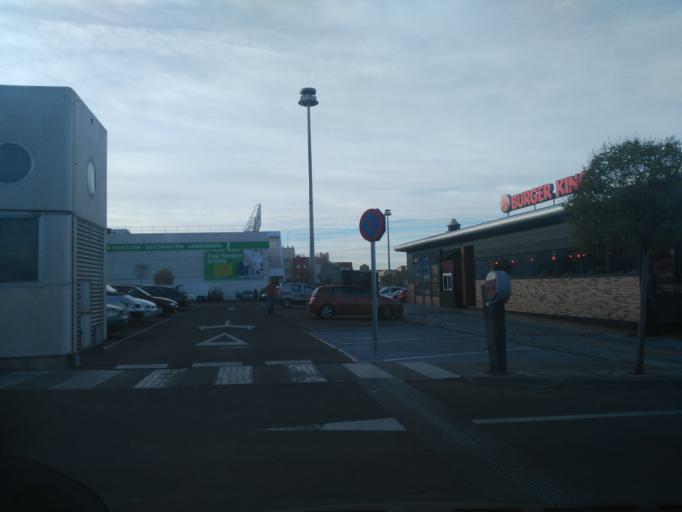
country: ES
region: Castille and Leon
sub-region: Provincia de Salamanca
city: Carbajosa de la Sagrada
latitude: 40.9489
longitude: -5.6507
